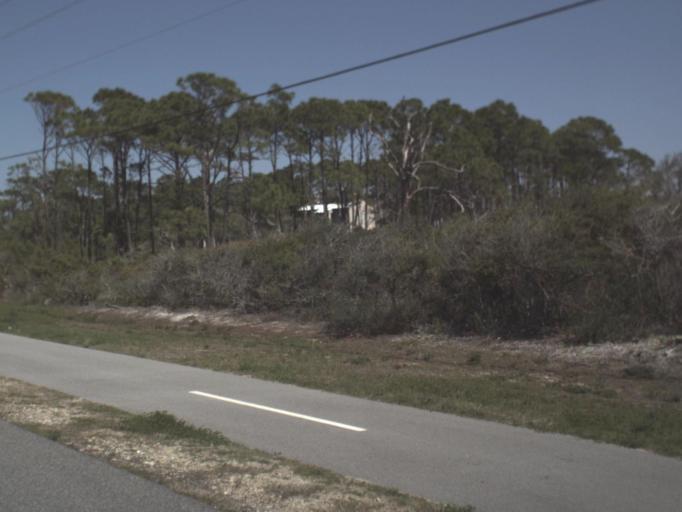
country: US
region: Florida
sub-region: Gulf County
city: Port Saint Joe
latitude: 29.6919
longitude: -85.3731
